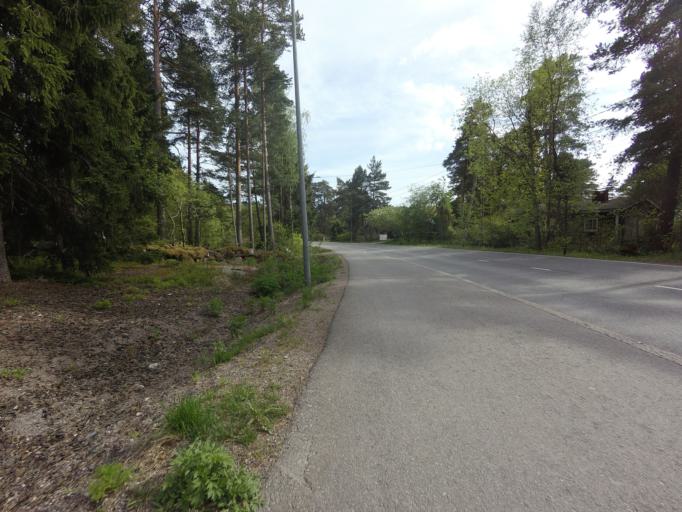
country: FI
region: Uusimaa
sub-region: Helsinki
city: Koukkuniemi
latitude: 60.1234
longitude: 24.7144
